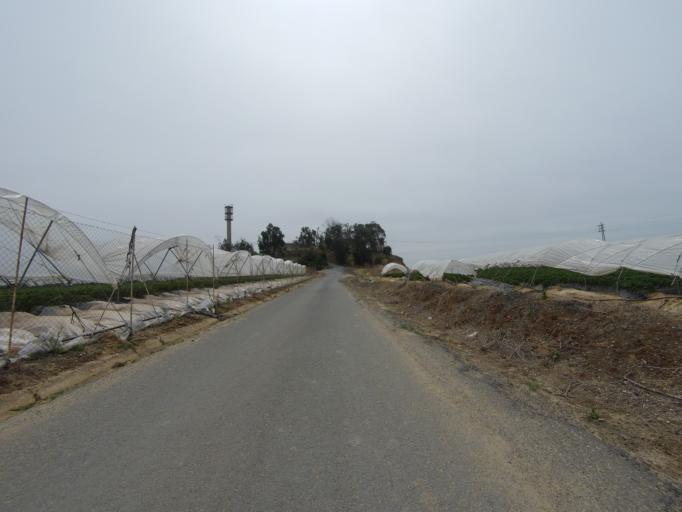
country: ES
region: Andalusia
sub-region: Provincia de Huelva
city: Palos de la Frontera
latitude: 37.2419
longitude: -6.8841
